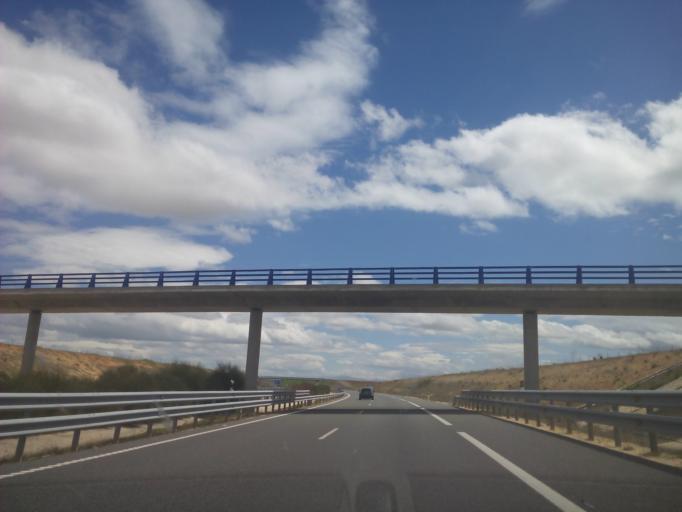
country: ES
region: Castille and Leon
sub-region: Provincia de Salamanca
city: Machacon
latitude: 40.9218
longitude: -5.5323
